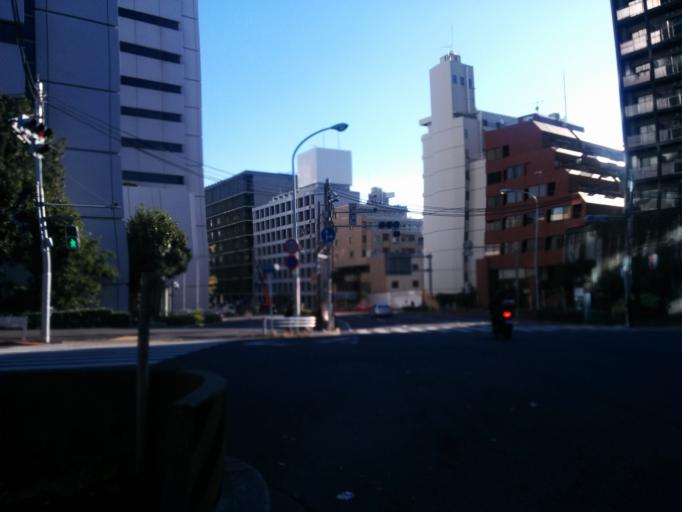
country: JP
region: Tokyo
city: Tokyo
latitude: 35.6804
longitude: 139.7045
